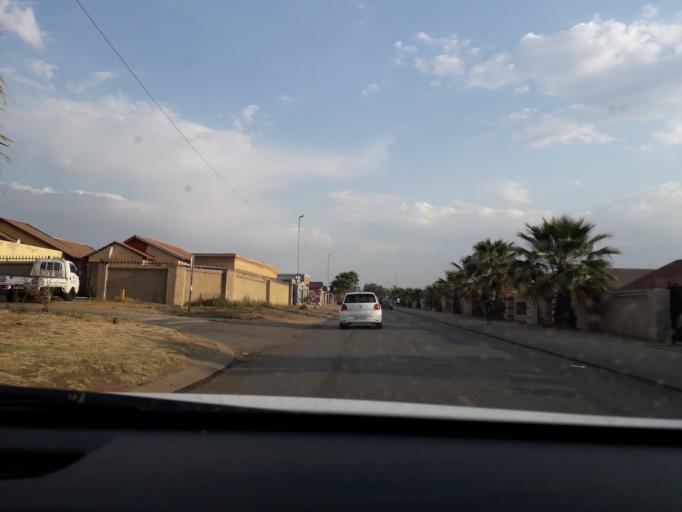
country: ZA
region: Gauteng
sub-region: Ekurhuleni Metropolitan Municipality
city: Tembisa
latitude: -26.0424
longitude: 28.1959
